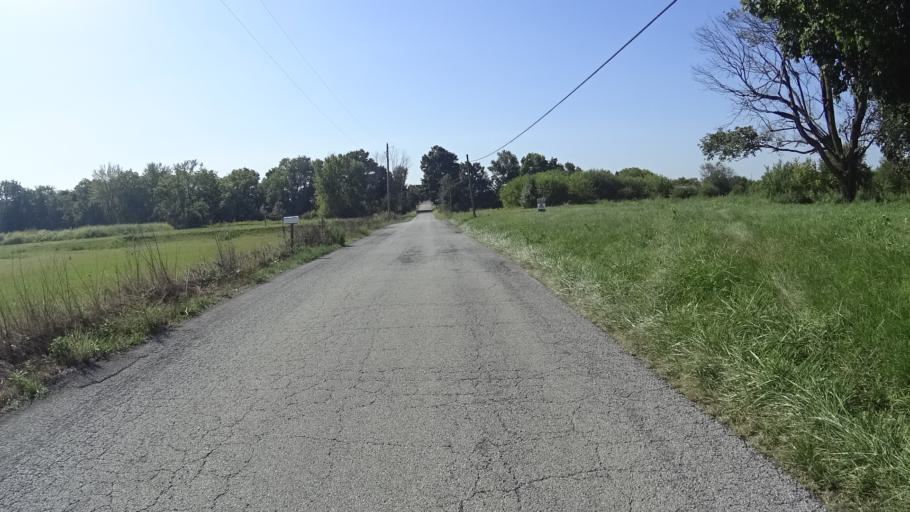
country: US
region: Indiana
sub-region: Madison County
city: Lapel
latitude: 40.0637
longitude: -85.8535
